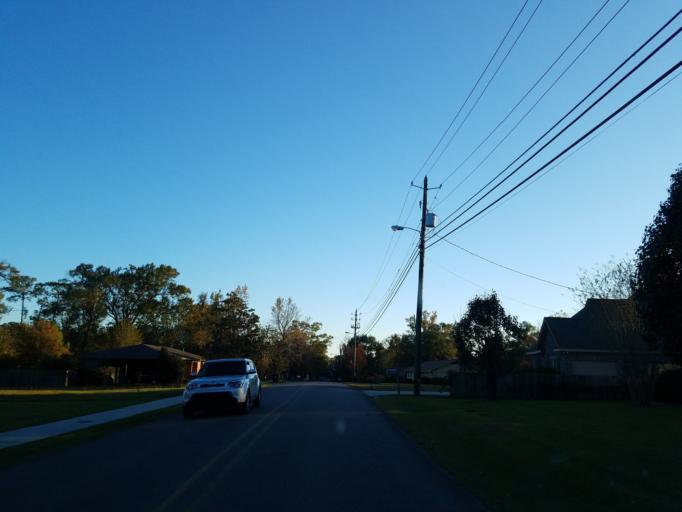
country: US
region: Mississippi
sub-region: Lamar County
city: West Hattiesburg
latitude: 31.3234
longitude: -89.3401
